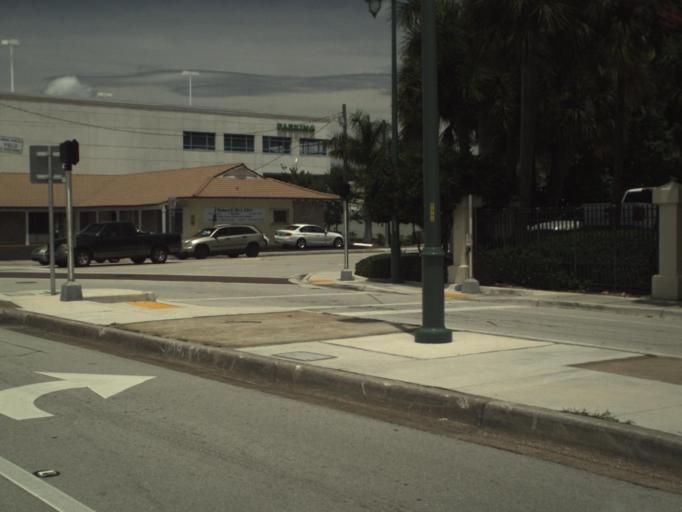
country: US
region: Florida
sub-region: Palm Beach County
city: Riviera Beach
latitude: 26.7833
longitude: -80.0495
